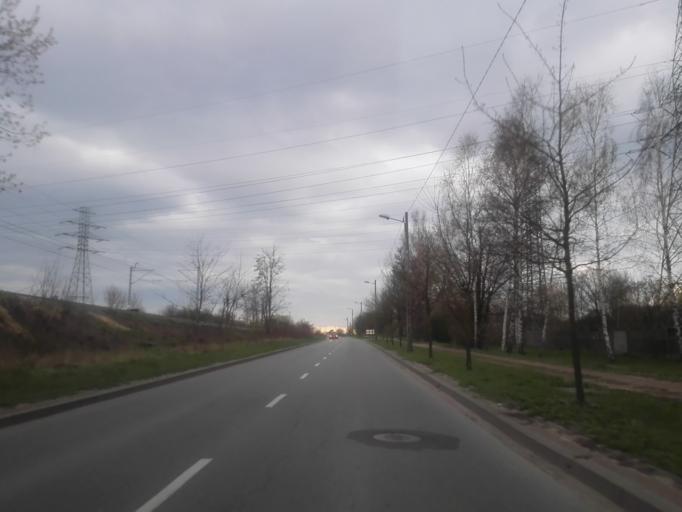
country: PL
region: Silesian Voivodeship
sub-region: Czestochowa
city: Czestochowa
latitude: 50.8316
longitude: 19.1430
